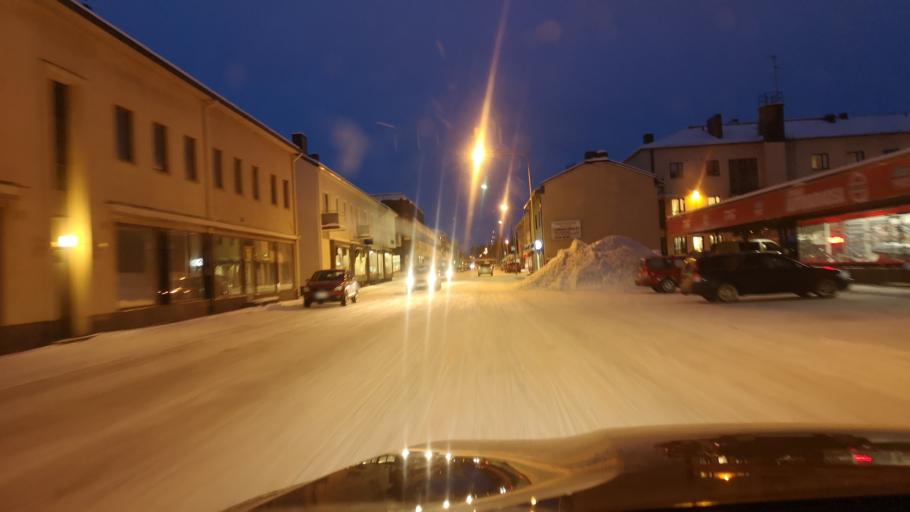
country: FI
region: Varsinais-Suomi
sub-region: Loimaa
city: Loimaa
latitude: 60.8520
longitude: 23.0610
